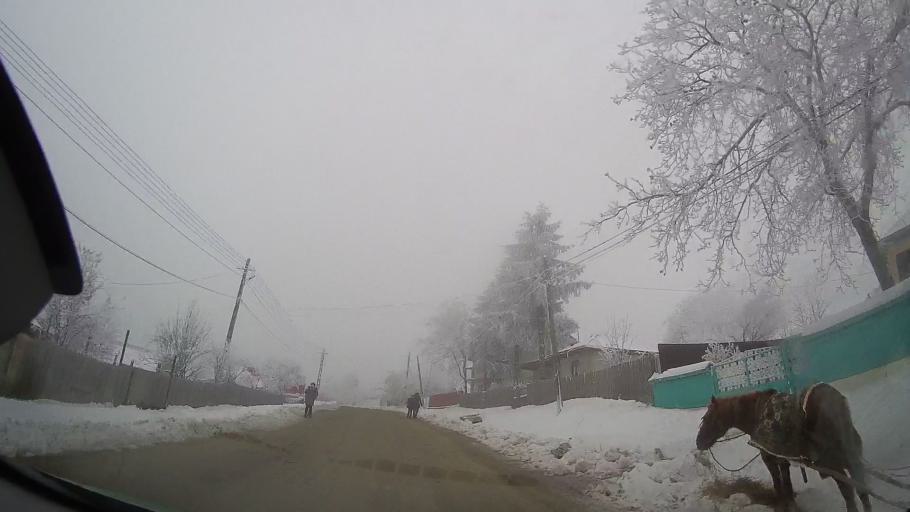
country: RO
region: Neamt
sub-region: Comuna Valea Ursului
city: Valea Ursului
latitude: 46.7992
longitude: 27.0799
